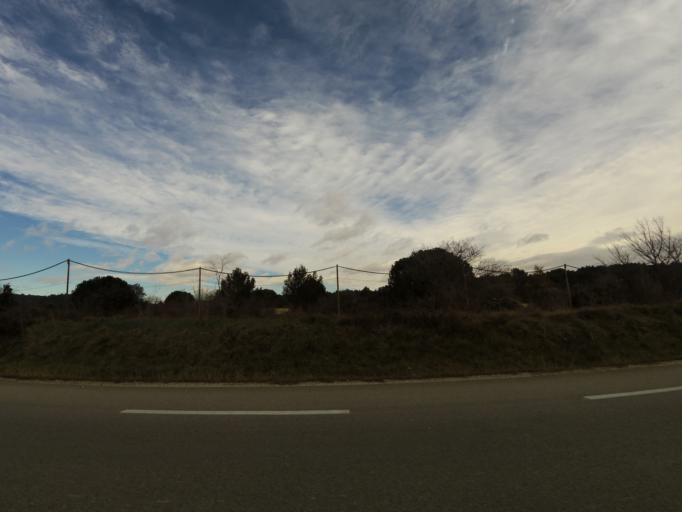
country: FR
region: Languedoc-Roussillon
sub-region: Departement du Gard
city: Caveirac
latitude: 43.8224
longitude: 4.2784
